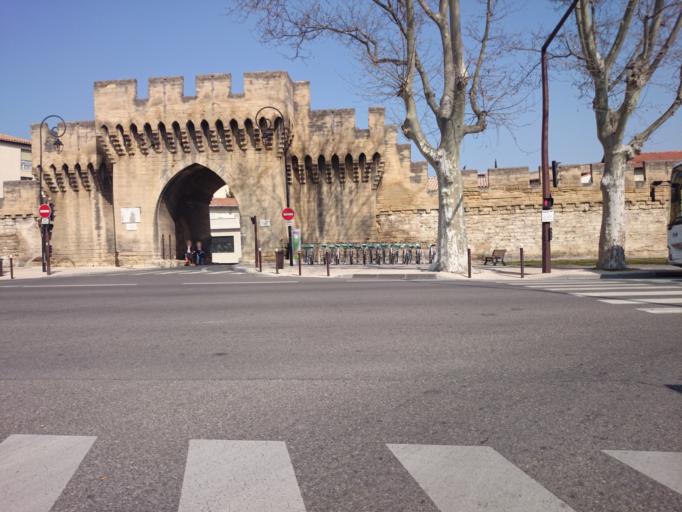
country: FR
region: Provence-Alpes-Cote d'Azur
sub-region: Departement du Vaucluse
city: Avignon
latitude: 43.9433
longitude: 4.7993
